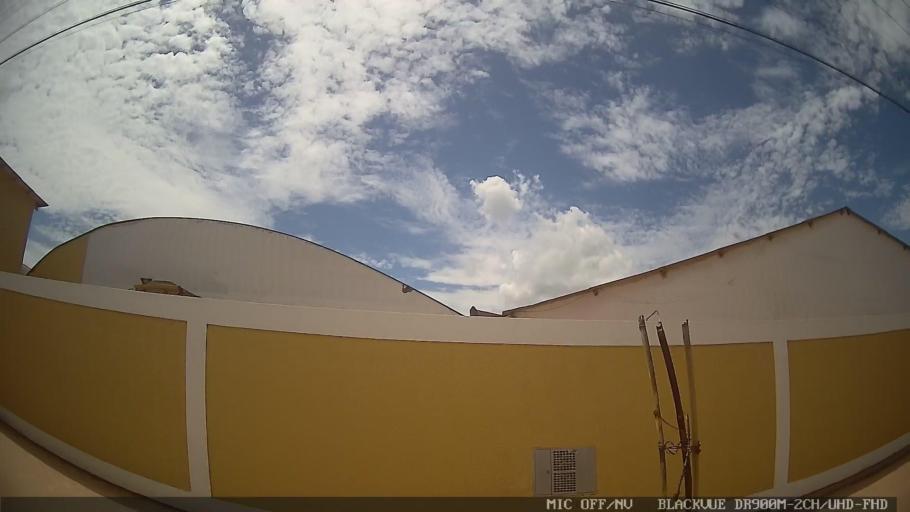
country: BR
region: Sao Paulo
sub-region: Conchas
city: Conchas
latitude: -23.0868
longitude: -47.9786
